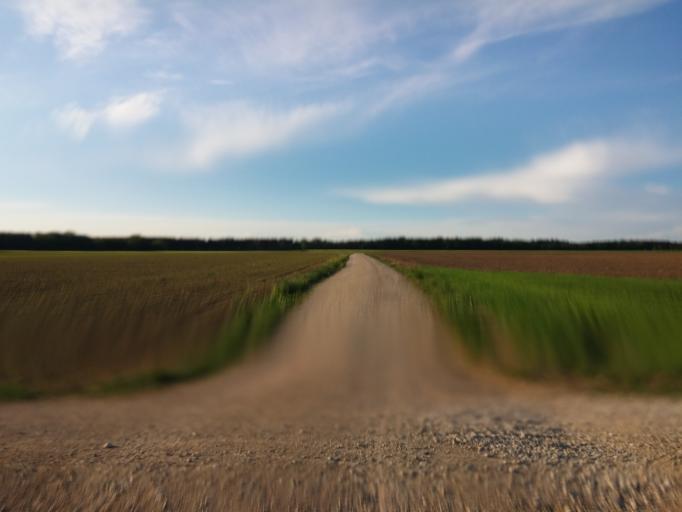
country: DE
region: Bavaria
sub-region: Upper Bavaria
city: Zorneding
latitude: 48.1044
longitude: 11.8183
